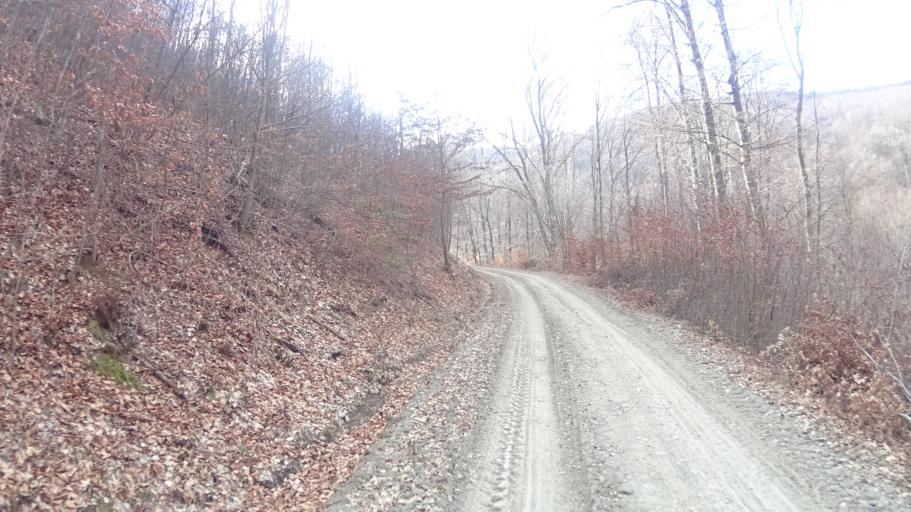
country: HU
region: Heves
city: Szilvasvarad
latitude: 48.0731
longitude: 20.4070
